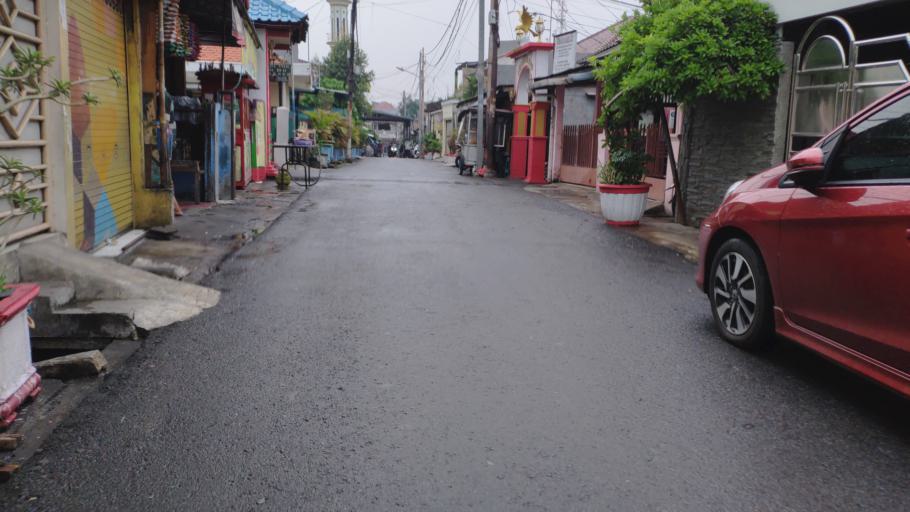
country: ID
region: Jakarta Raya
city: Jakarta
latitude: -6.2075
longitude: 106.8705
